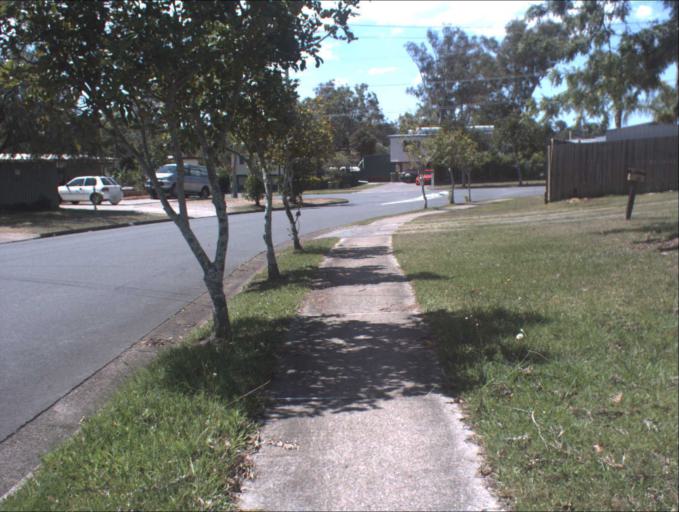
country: AU
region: Queensland
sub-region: Logan
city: Logan City
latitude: -27.6568
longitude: 153.0933
